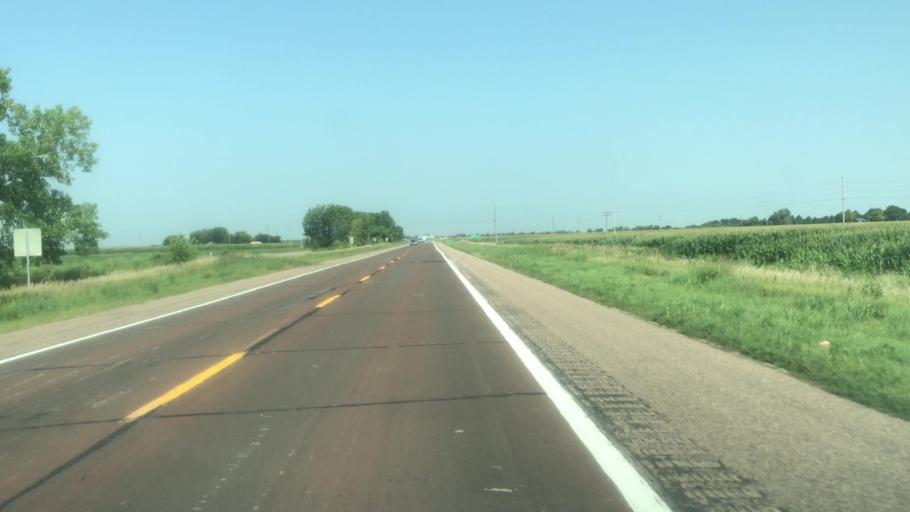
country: US
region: Nebraska
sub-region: Hall County
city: Grand Island
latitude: 40.9731
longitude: -98.5084
